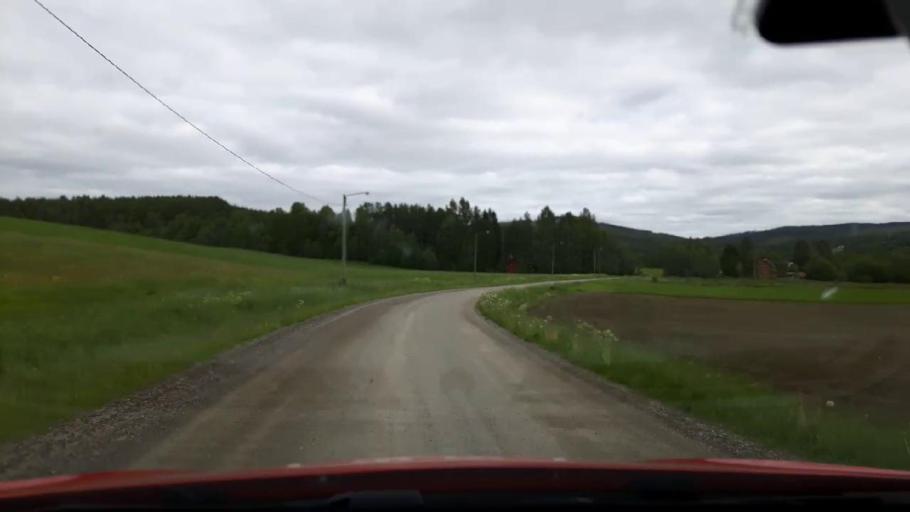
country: SE
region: Jaemtland
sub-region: Ragunda Kommun
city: Hammarstrand
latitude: 63.1565
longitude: 16.2390
